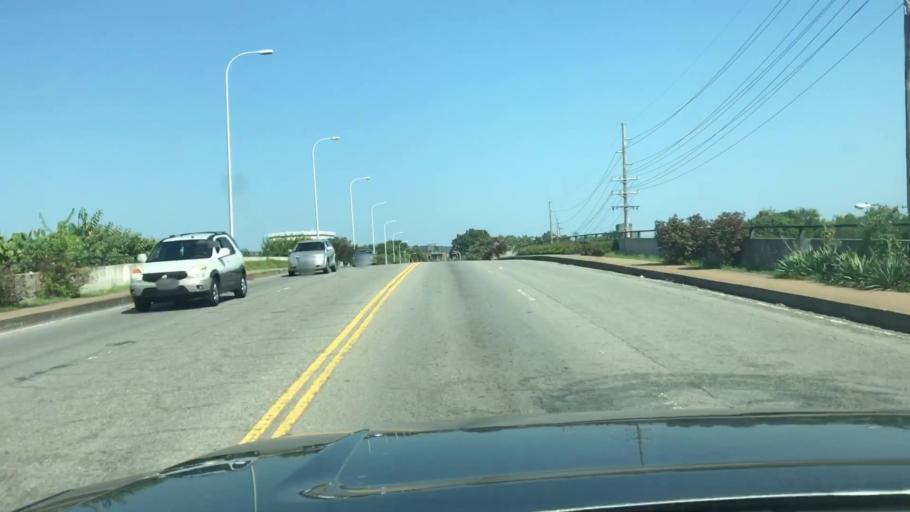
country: US
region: Tennessee
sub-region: Davidson County
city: Nashville
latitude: 36.1617
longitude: -86.8026
